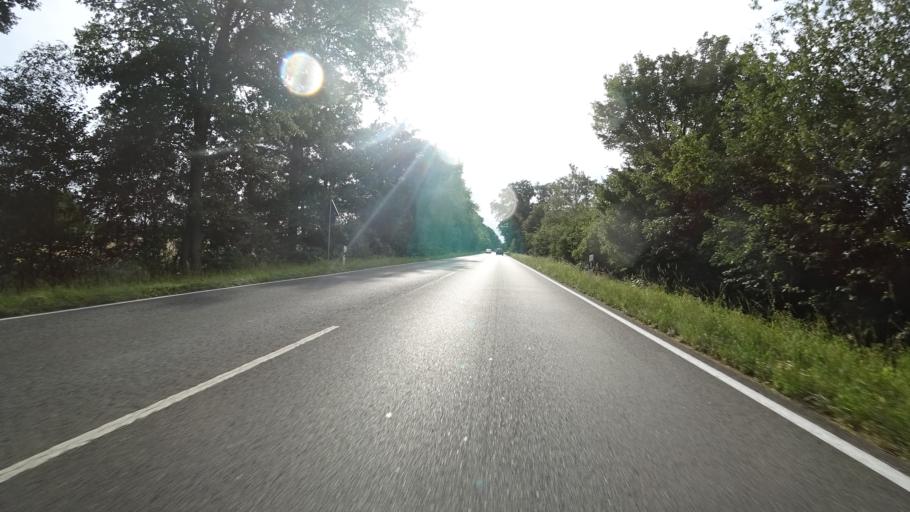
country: DE
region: North Rhine-Westphalia
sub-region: Regierungsbezirk Munster
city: Beelen
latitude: 51.9713
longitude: 8.1645
